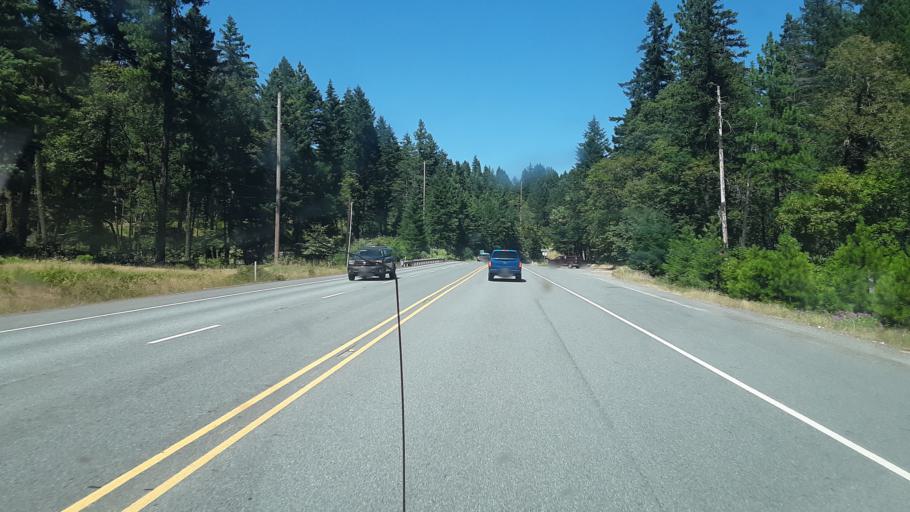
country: US
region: Oregon
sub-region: Josephine County
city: Cave Junction
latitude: 42.3321
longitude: -123.5896
